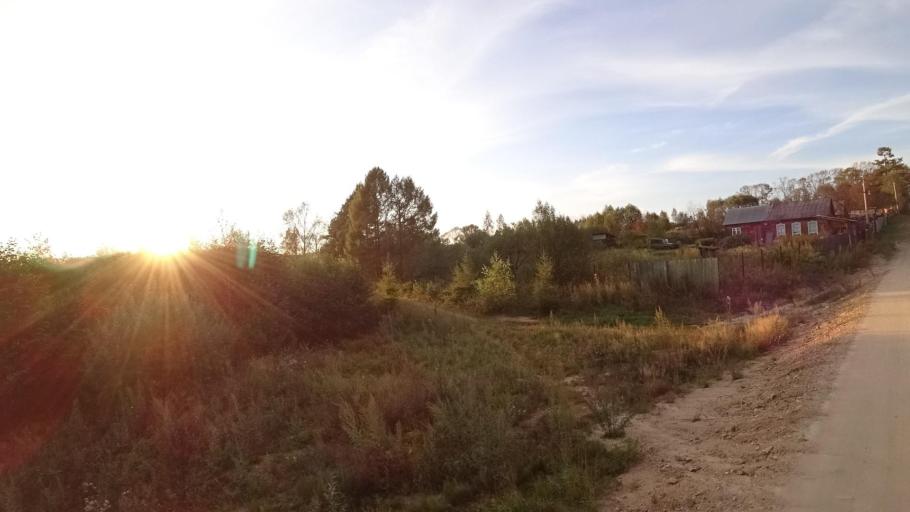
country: RU
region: Jewish Autonomous Oblast
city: Kul'dur
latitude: 49.2064
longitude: 131.6401
